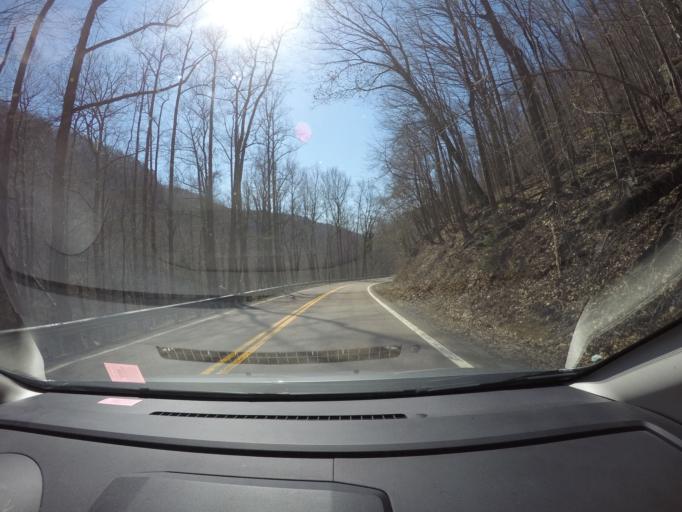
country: US
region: Tennessee
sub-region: Hamilton County
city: Signal Mountain
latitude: 35.1447
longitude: -85.3888
